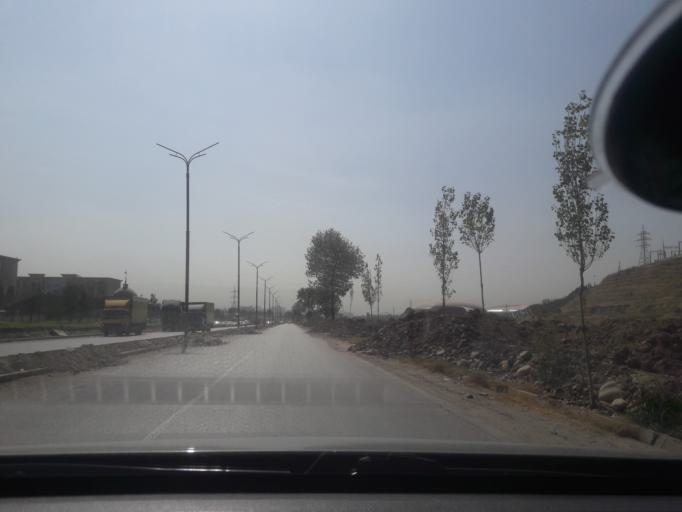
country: TJ
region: Dushanbe
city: Dushanbe
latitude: 38.6082
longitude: 68.7714
